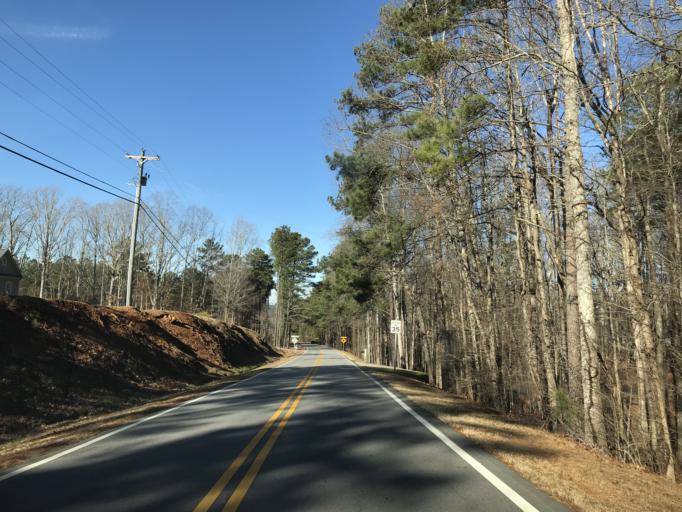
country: US
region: Georgia
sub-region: Paulding County
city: Dallas
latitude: 33.9789
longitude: -84.8779
